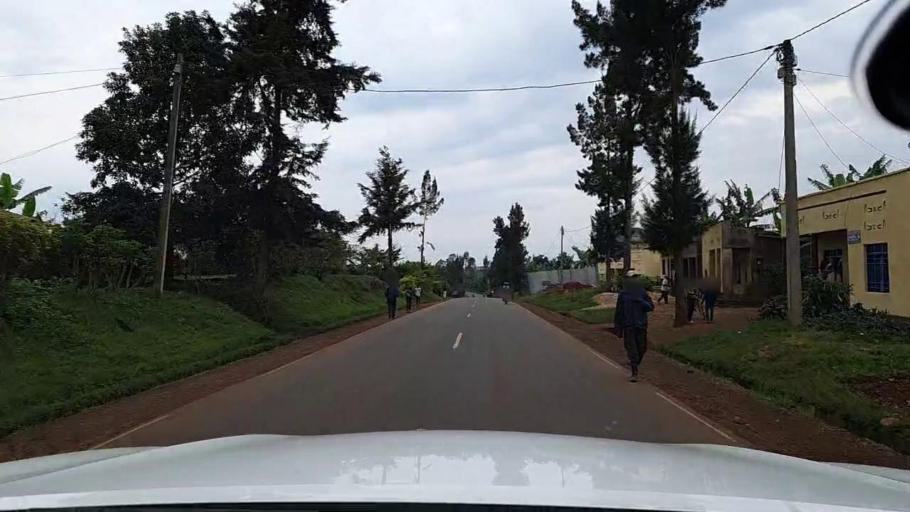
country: RW
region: Western Province
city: Cyangugu
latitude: -2.6060
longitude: 28.9341
